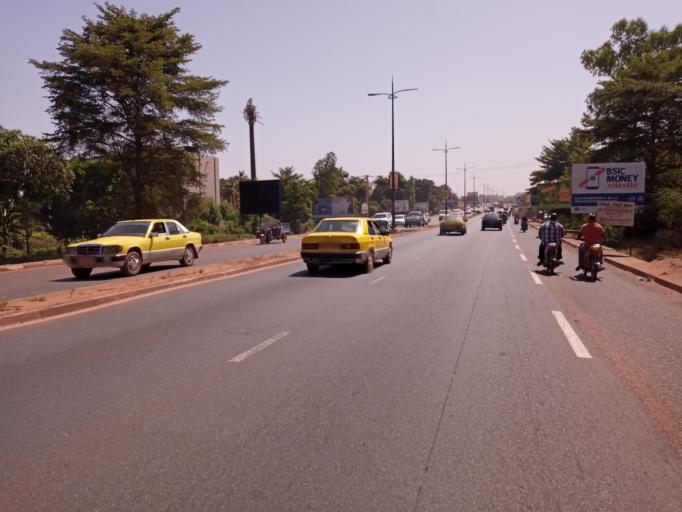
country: ML
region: Bamako
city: Bamako
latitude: 12.6182
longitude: -8.0010
